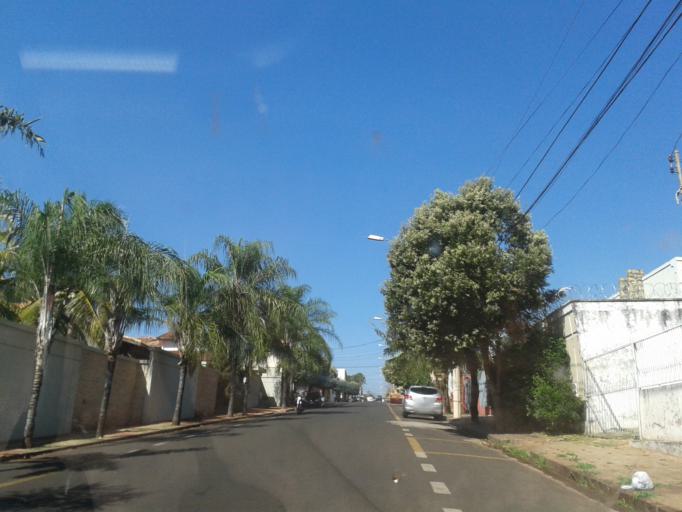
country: BR
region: Minas Gerais
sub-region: Ituiutaba
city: Ituiutaba
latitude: -18.9760
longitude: -49.4575
